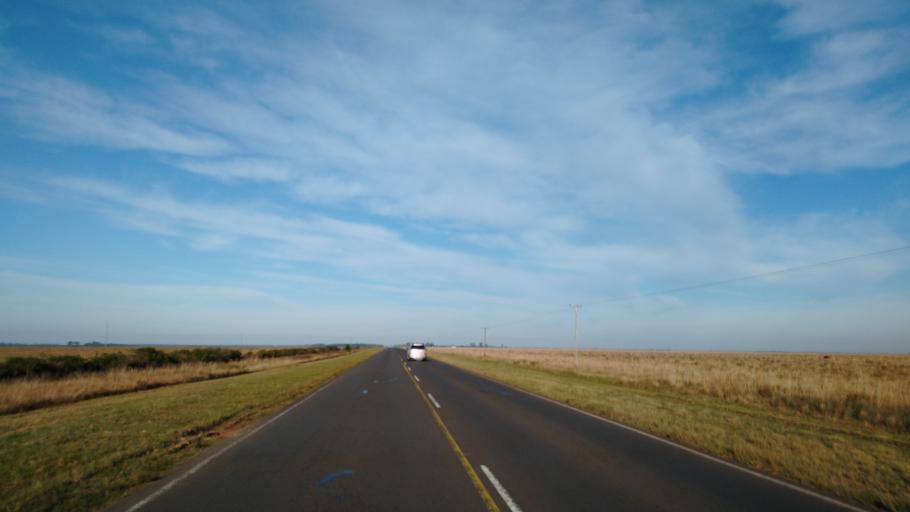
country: AR
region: Corrientes
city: La Cruz
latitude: -29.2123
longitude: -56.7030
